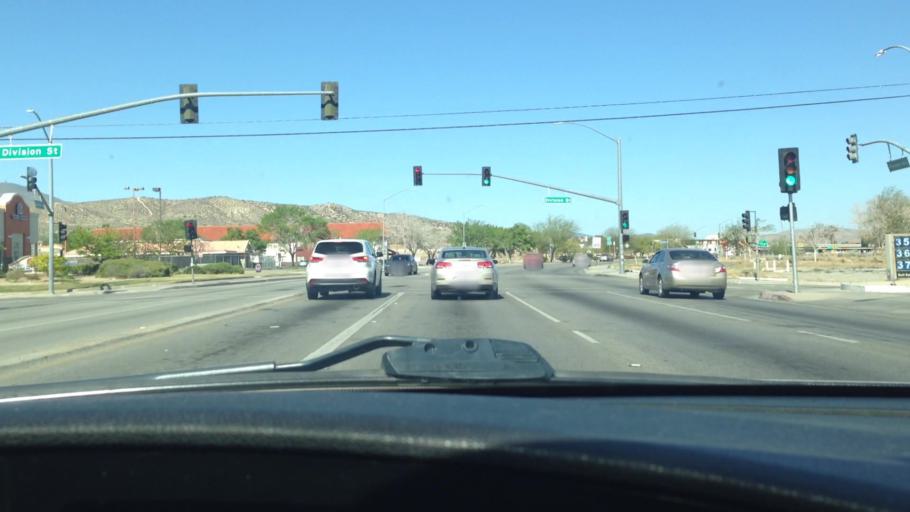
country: US
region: California
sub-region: Los Angeles County
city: Palmdale
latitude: 34.5799
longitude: -118.1291
